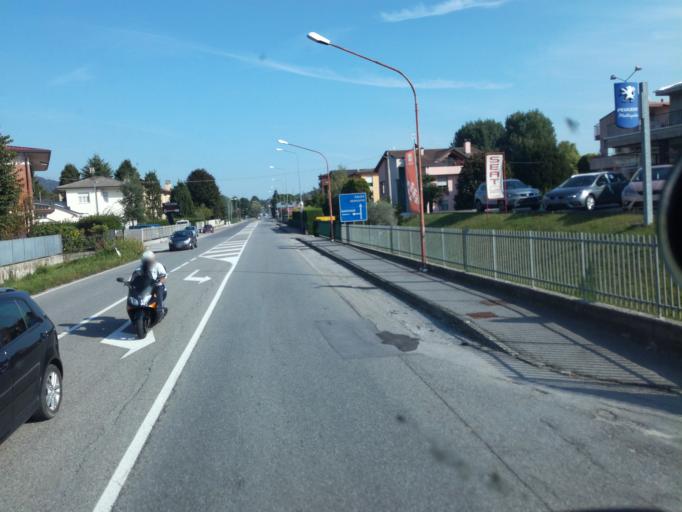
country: IT
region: Lombardy
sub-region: Provincia di Lecco
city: Barzago
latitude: 45.7544
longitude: 9.3122
